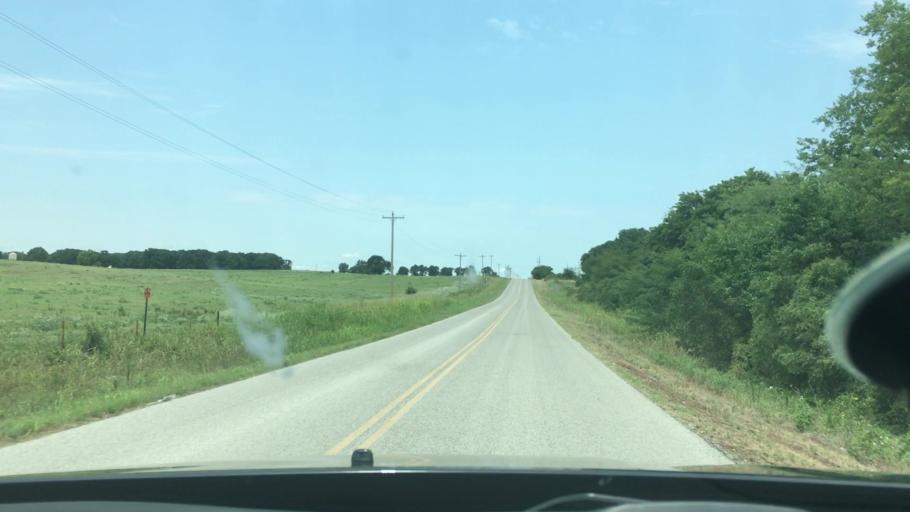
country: US
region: Oklahoma
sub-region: Love County
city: Marietta
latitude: 33.9046
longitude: -97.3521
